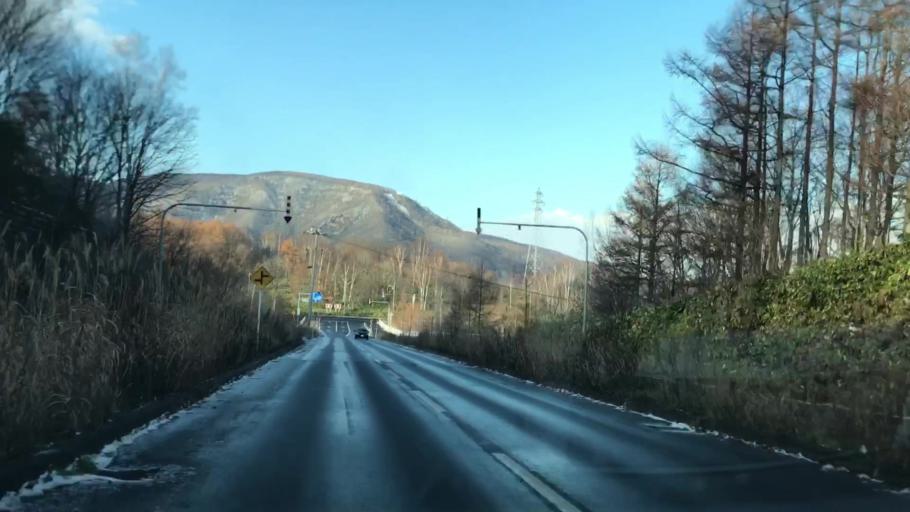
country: JP
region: Hokkaido
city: Otaru
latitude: 43.1674
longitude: 141.0093
